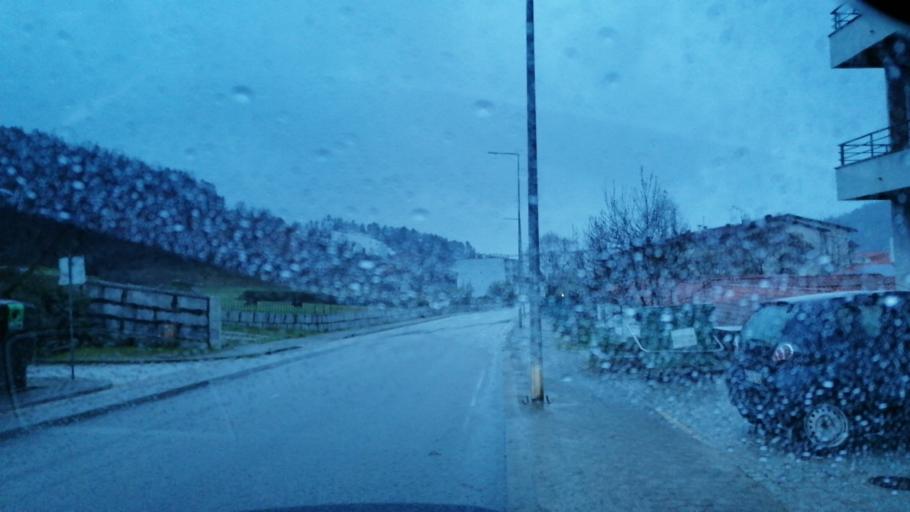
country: PT
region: Vila Real
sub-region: Vila Pouca de Aguiar
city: Vila Pouca de Aguiar
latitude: 41.4969
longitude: -7.6423
